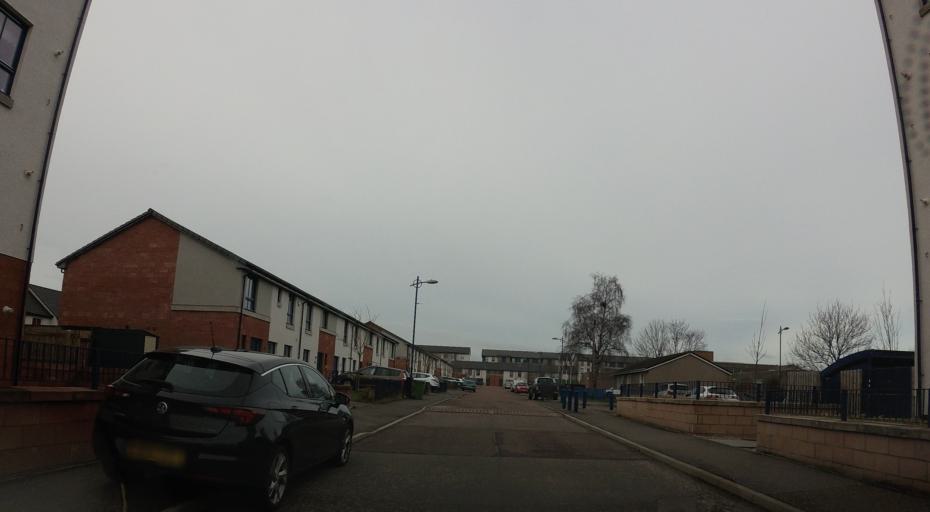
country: GB
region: Scotland
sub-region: South Lanarkshire
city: Rutherglen
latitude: 55.8411
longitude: -4.2388
